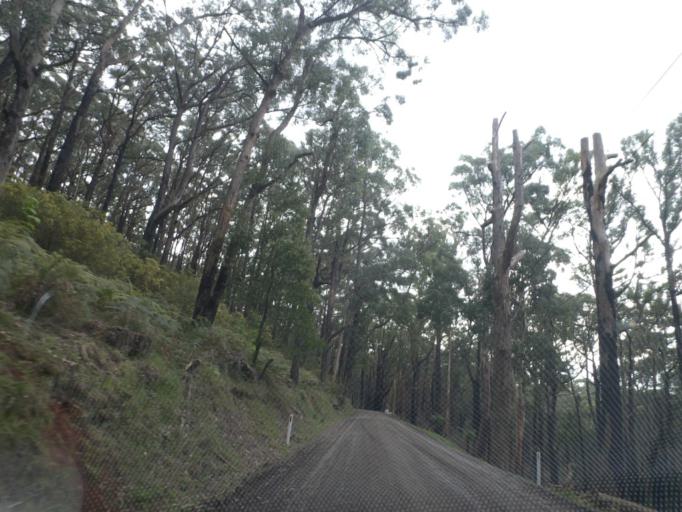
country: AU
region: Victoria
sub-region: Yarra Ranges
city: Olinda
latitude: -37.8540
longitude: 145.3555
